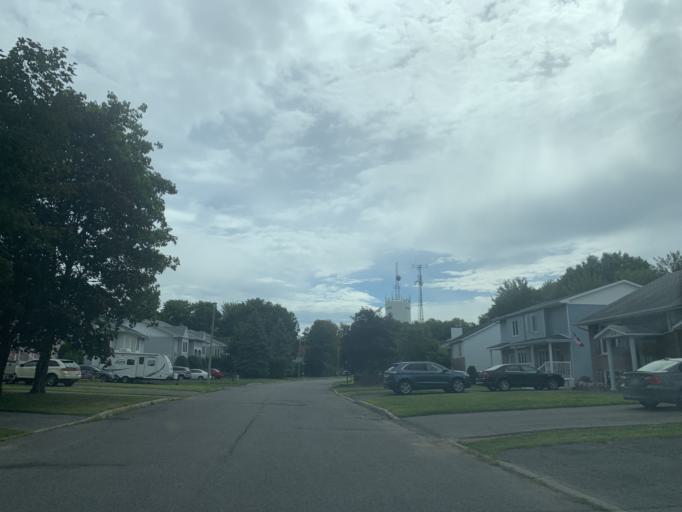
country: CA
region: Ontario
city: Hawkesbury
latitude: 45.5972
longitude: -74.6078
